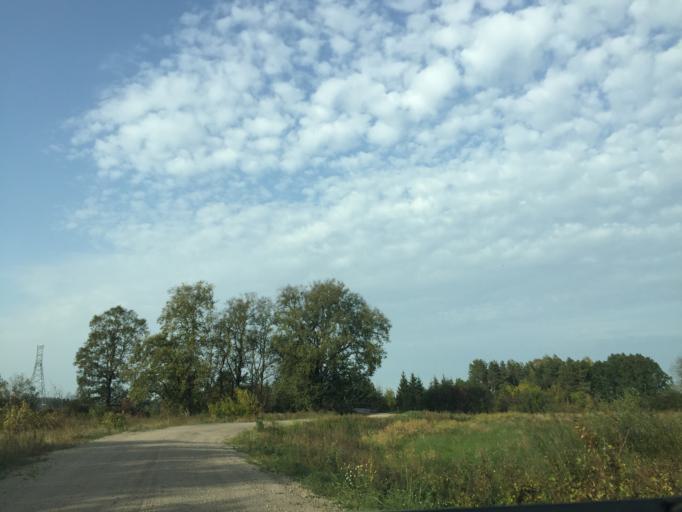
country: LV
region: Garkalne
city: Garkalne
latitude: 56.9752
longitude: 24.4195
